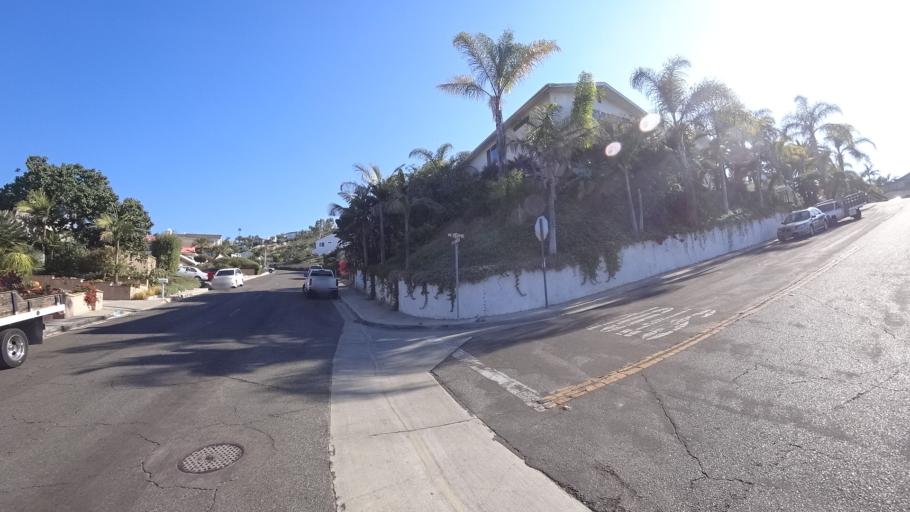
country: US
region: California
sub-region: Orange County
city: San Clemente
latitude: 33.4171
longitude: -117.5999
